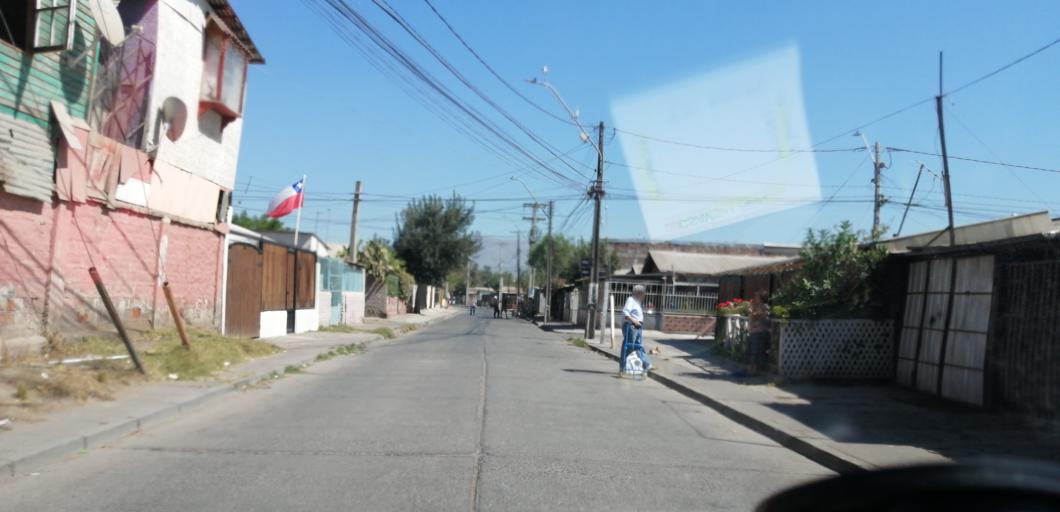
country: CL
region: Santiago Metropolitan
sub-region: Provincia de Santiago
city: Lo Prado
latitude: -33.4332
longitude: -70.7562
